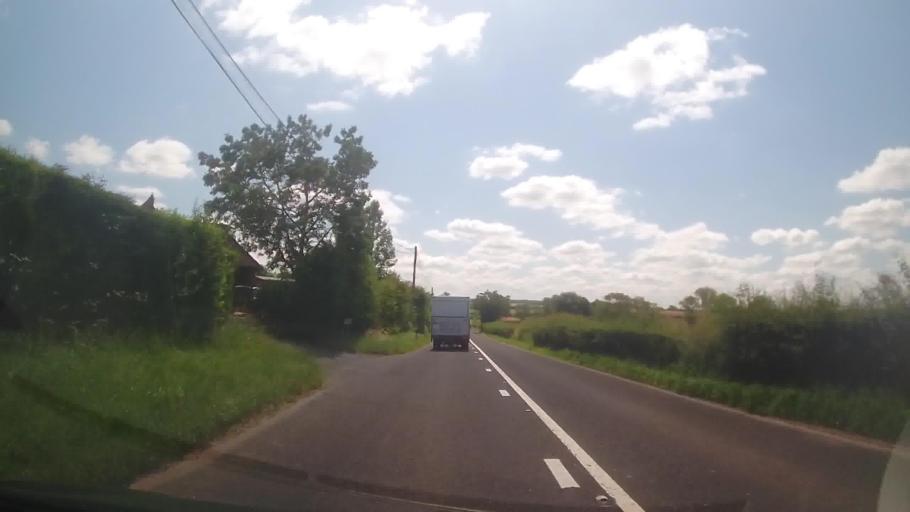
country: GB
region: England
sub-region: Herefordshire
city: Ocle Pychard
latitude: 52.1302
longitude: -2.6032
